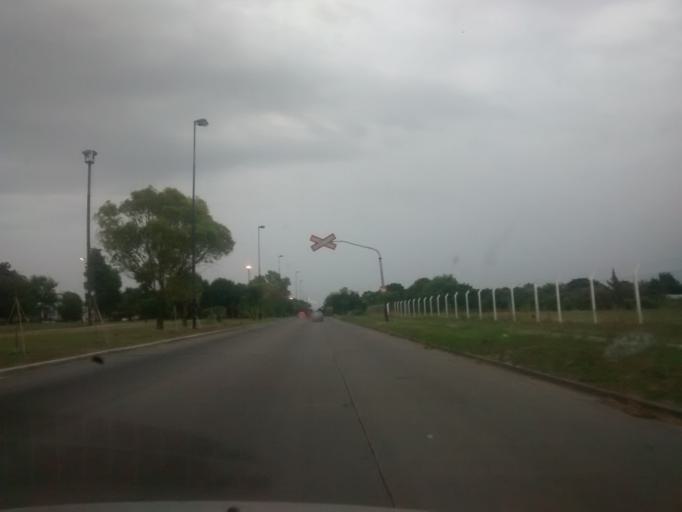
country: AR
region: Buenos Aires
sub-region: Partido de La Plata
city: La Plata
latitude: -34.9440
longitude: -57.9420
